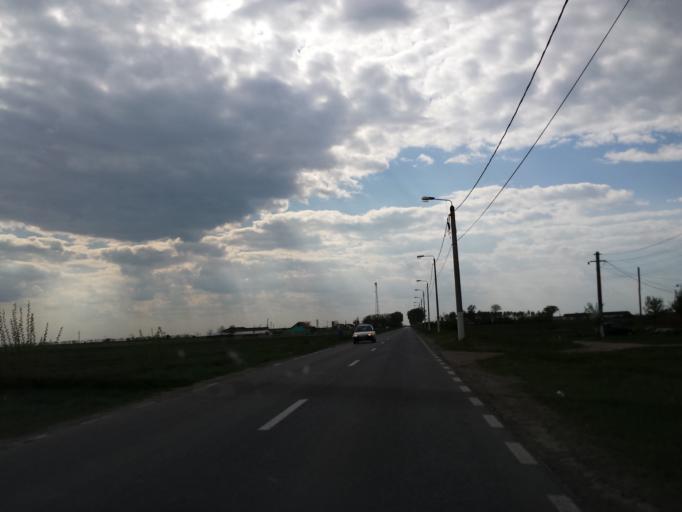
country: RO
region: Timis
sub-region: Comuna Cenad
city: Cenad
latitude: 46.1289
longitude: 20.5636
